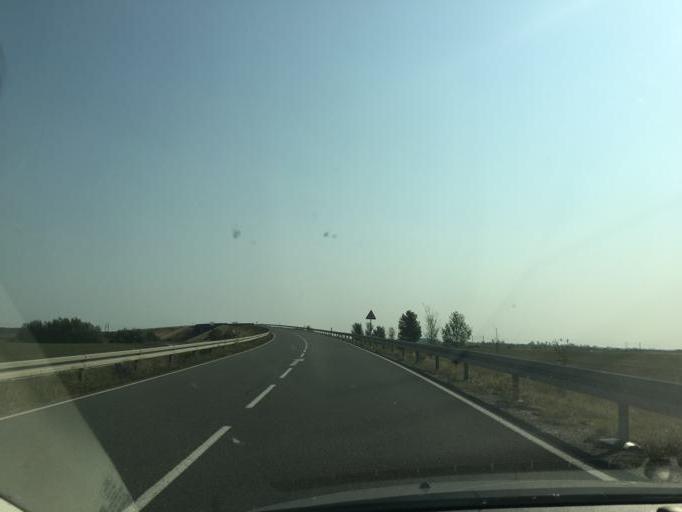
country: DE
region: Saxony-Anhalt
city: Schonebeck
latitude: 51.9897
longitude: 11.7641
